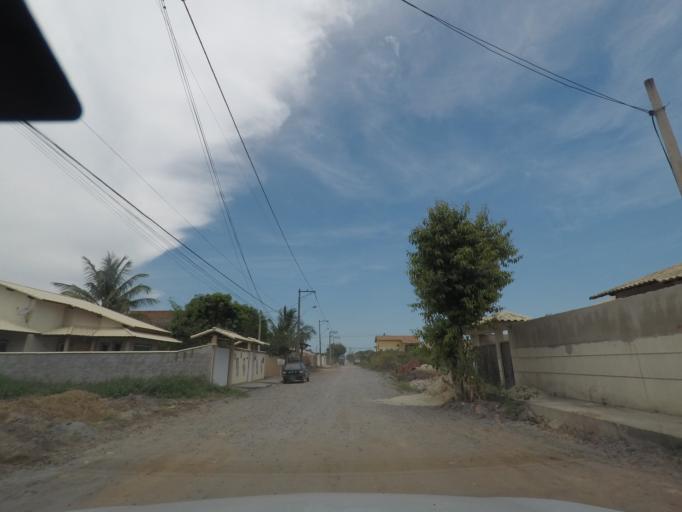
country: BR
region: Rio de Janeiro
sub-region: Marica
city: Marica
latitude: -22.9609
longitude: -42.9505
